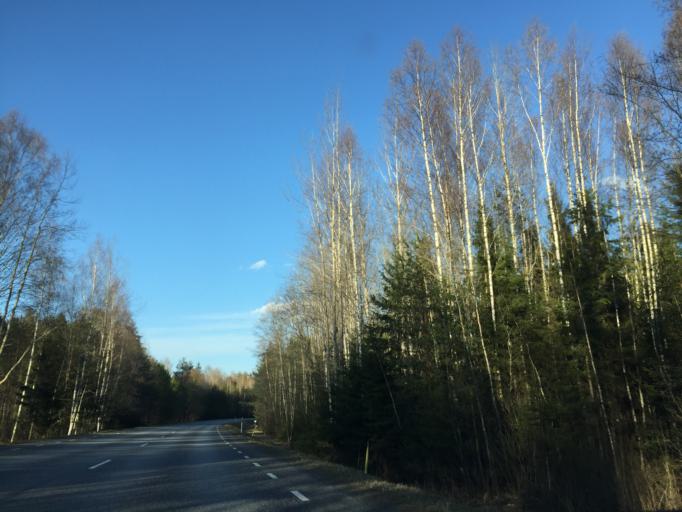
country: EE
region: Valgamaa
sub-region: Torva linn
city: Torva
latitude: 58.1257
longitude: 26.1399
